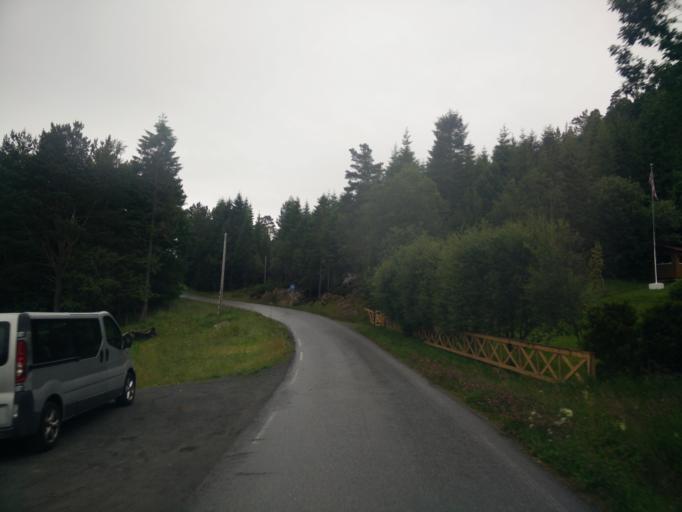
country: NO
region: More og Romsdal
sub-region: Kristiansund
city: Rensvik
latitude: 63.0210
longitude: 7.8981
